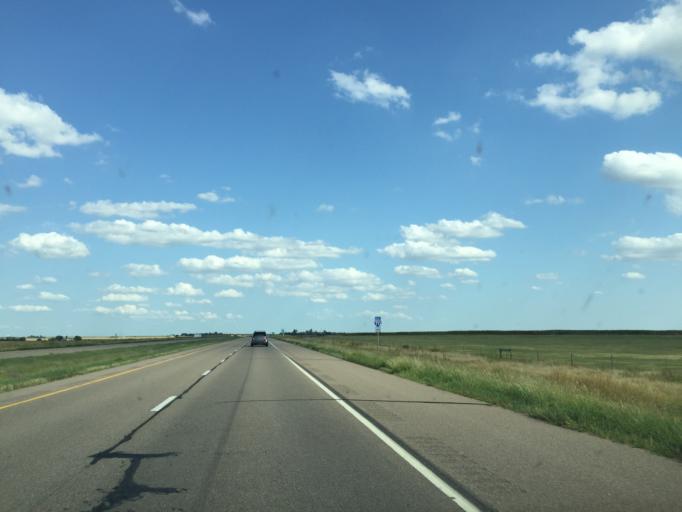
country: US
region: Kansas
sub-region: Gove County
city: Gove
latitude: 39.0551
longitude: -100.2359
